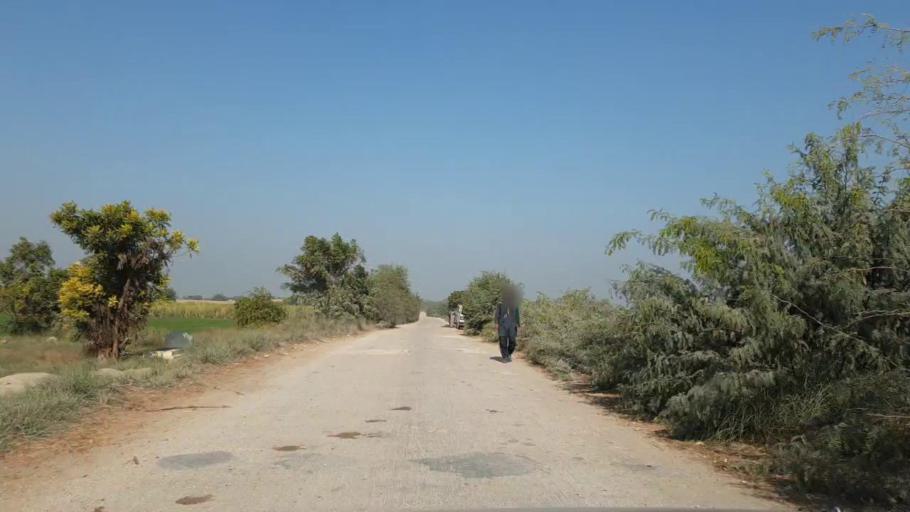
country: PK
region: Sindh
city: Matiari
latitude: 25.5804
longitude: 68.6036
